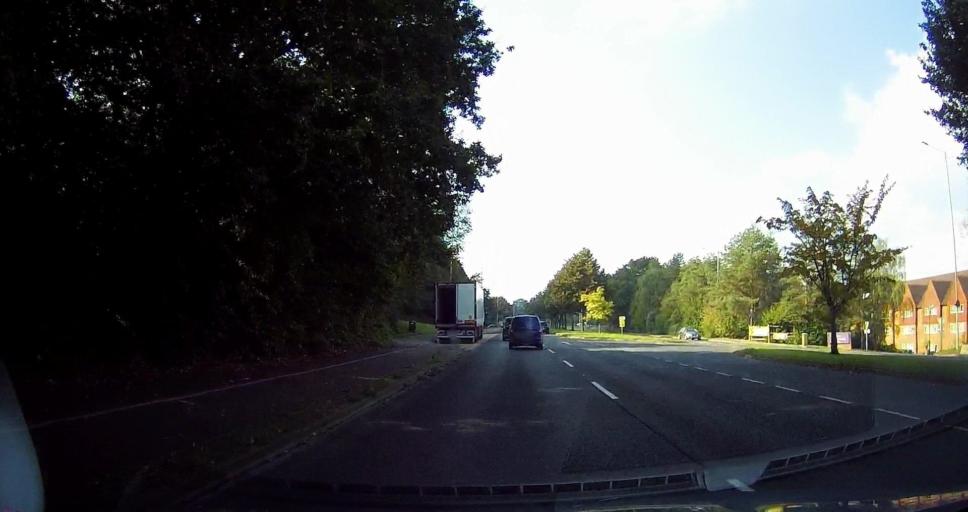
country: GB
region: England
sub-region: Kent
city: Ashford
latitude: 51.1572
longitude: 0.8661
